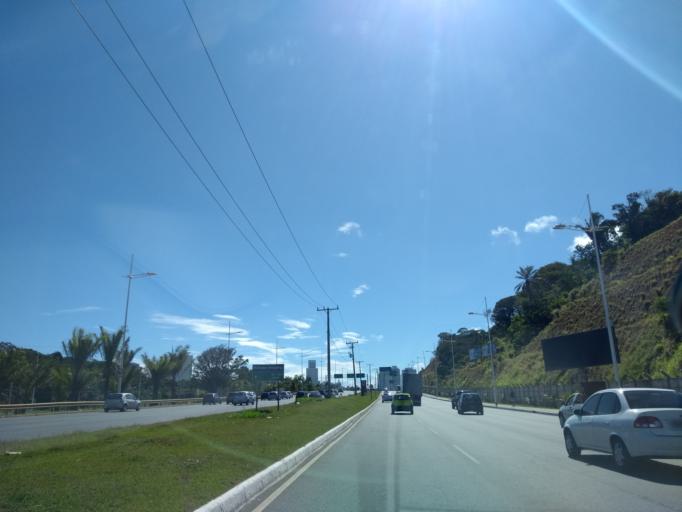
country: BR
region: Bahia
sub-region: Salvador
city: Salvador
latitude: -12.9704
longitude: -38.4448
